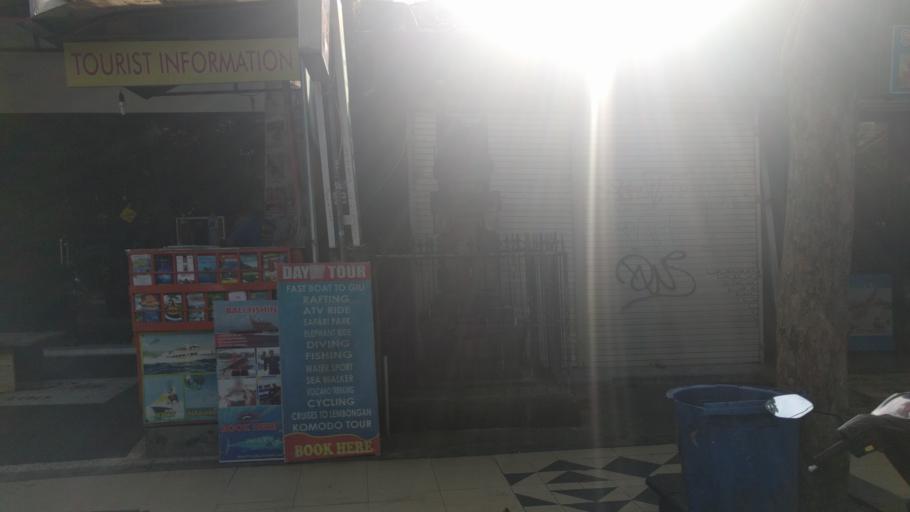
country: ID
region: Bali
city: Kuta
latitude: -8.7148
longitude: 115.1737
